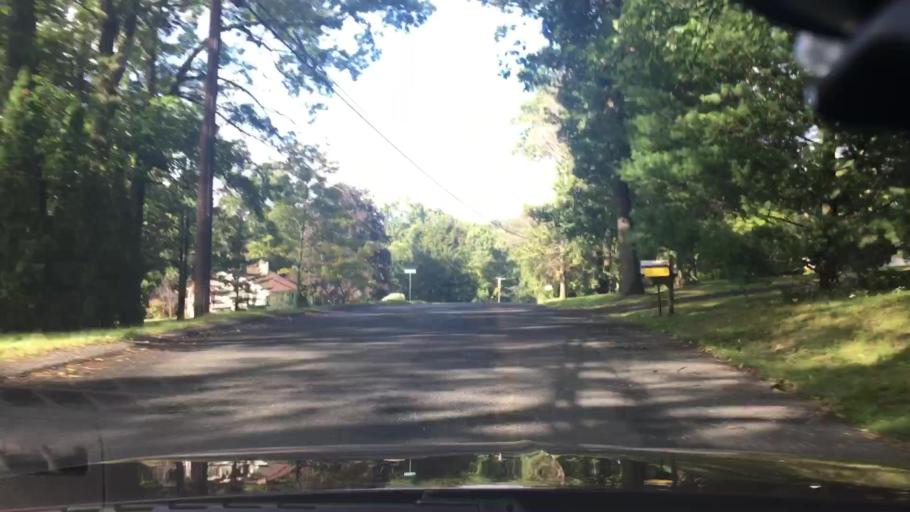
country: US
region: Connecticut
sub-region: Tolland County
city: Somers
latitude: 41.9725
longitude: -72.4135
